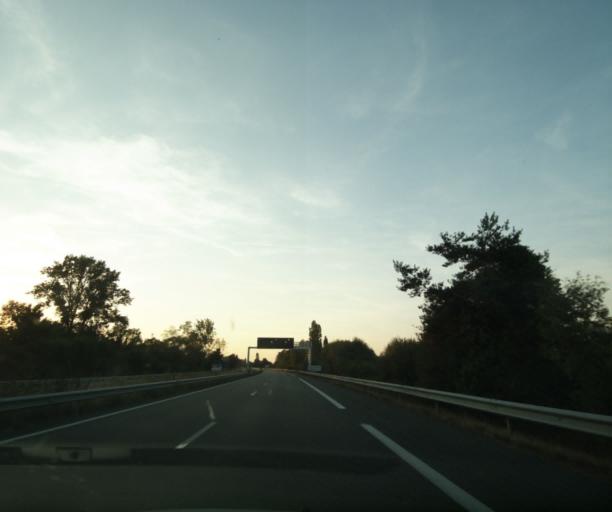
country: FR
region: Aquitaine
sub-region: Departement du Lot-et-Garonne
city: Fourques-sur-Garonne
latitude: 44.4217
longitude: 0.1694
